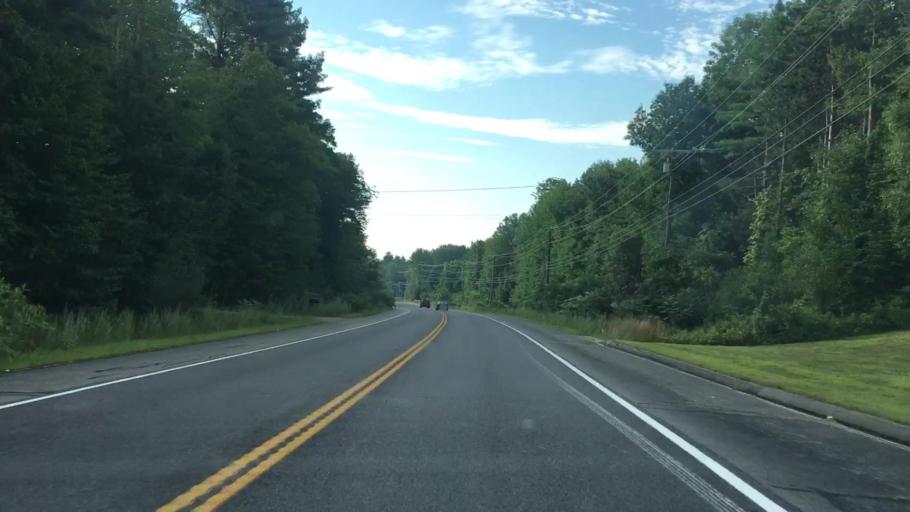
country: US
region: Maine
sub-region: Cumberland County
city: South Windham
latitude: 43.7647
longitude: -70.3751
